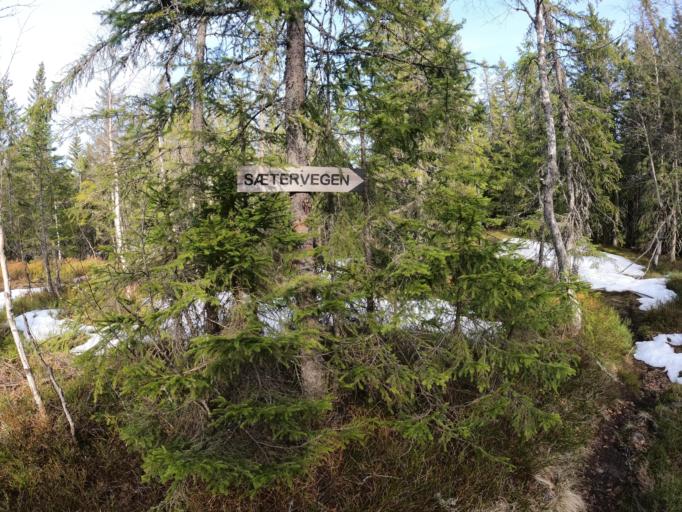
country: NO
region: Akershus
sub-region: Nannestad
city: Teigebyen
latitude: 60.2444
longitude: 10.9164
